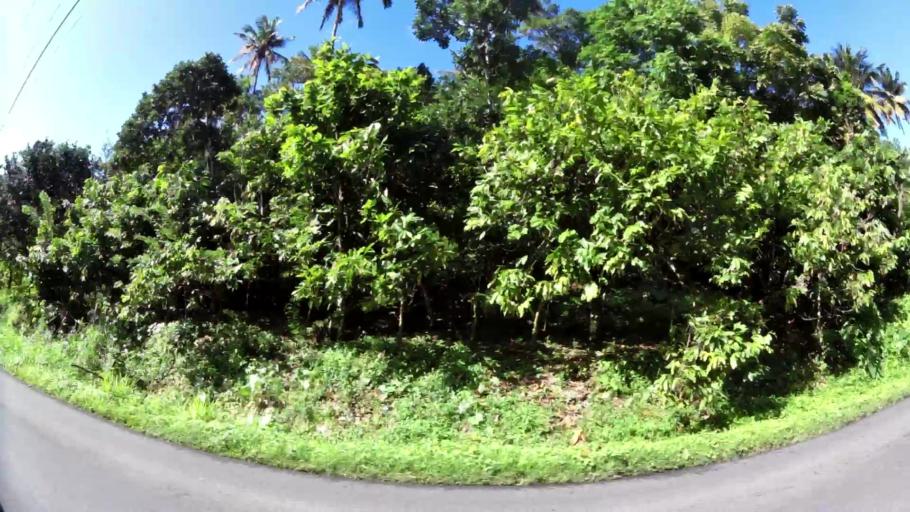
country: LC
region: Soufriere
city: Soufriere
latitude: 13.8269
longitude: -61.0488
